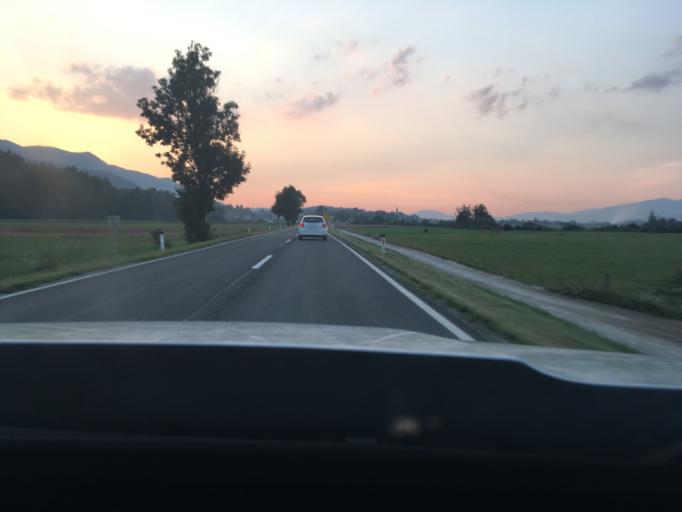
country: SI
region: Ribnica
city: Ribnica
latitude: 45.6959
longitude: 14.7666
